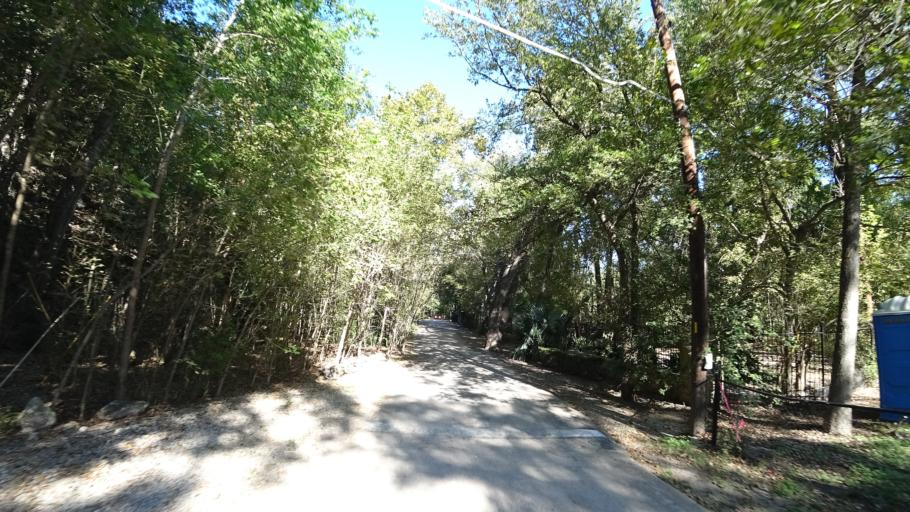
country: US
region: Texas
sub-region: Travis County
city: West Lake Hills
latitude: 30.3362
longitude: -97.7864
